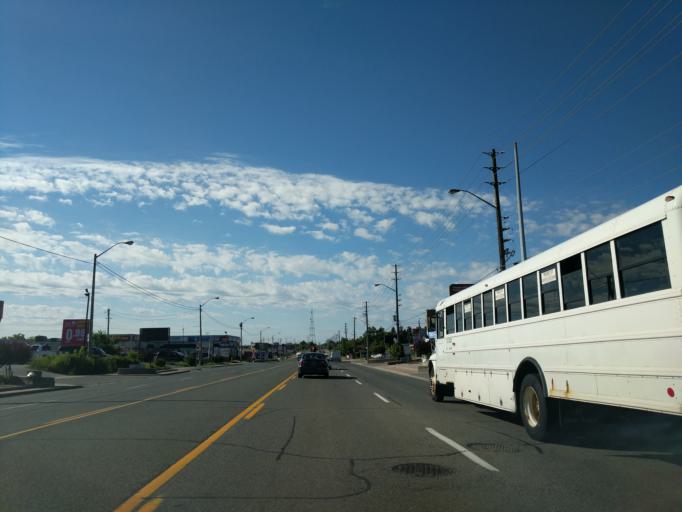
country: CA
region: Ontario
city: Scarborough
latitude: 43.7583
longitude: -79.2783
